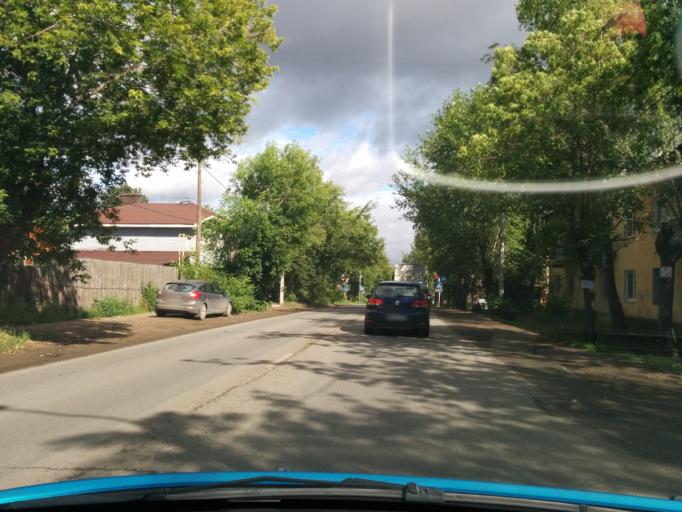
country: RU
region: Perm
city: Kondratovo
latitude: 58.0434
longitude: 56.1033
